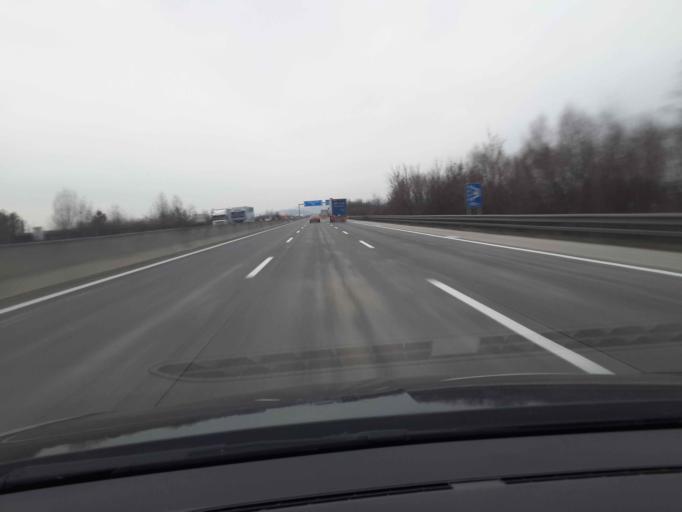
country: AT
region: Lower Austria
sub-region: Politischer Bezirk Amstetten
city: Sankt Valentin
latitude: 48.1880
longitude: 14.5331
